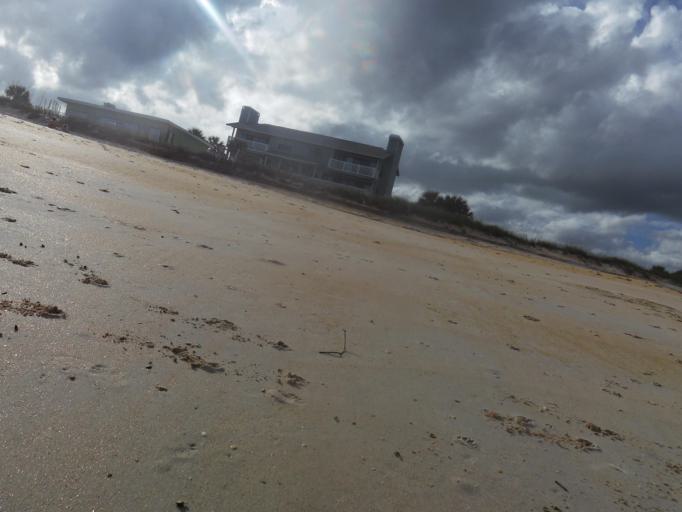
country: US
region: Florida
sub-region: Flagler County
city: Palm Coast
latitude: 29.6324
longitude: -81.1971
